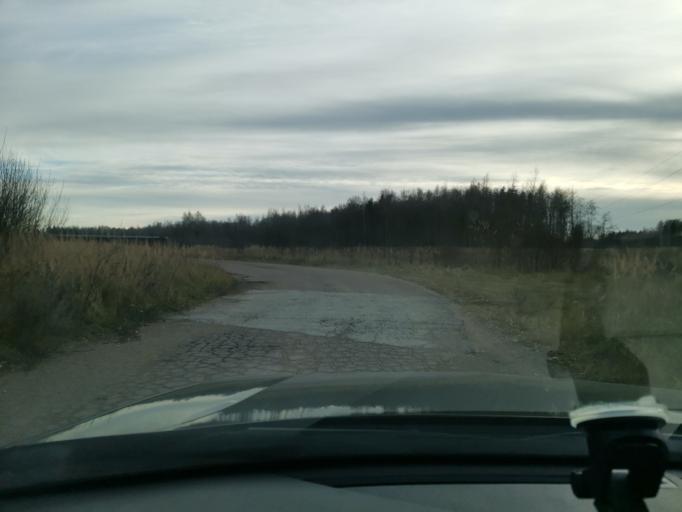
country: EE
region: Ida-Virumaa
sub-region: Sillamaee linn
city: Sillamae
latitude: 59.2620
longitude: 27.9066
